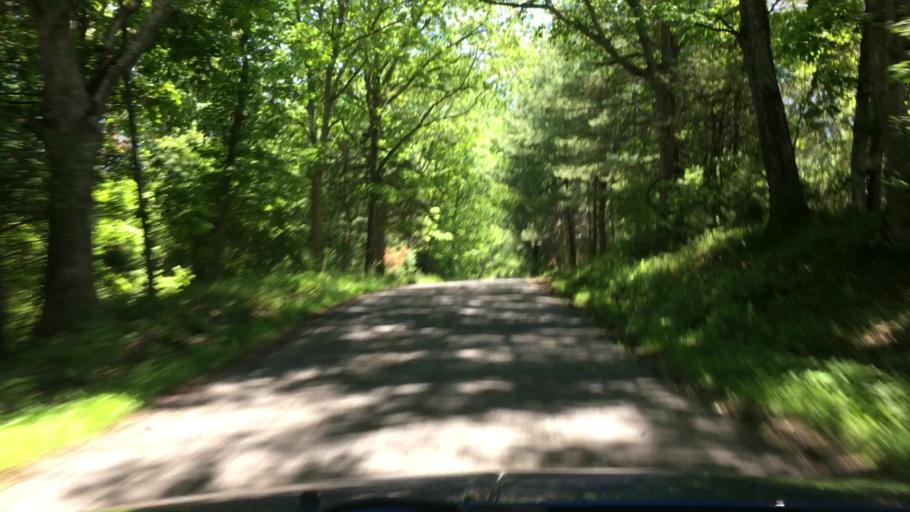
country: US
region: Virginia
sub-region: Bath County
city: Warm Springs
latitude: 38.0750
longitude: -79.5862
